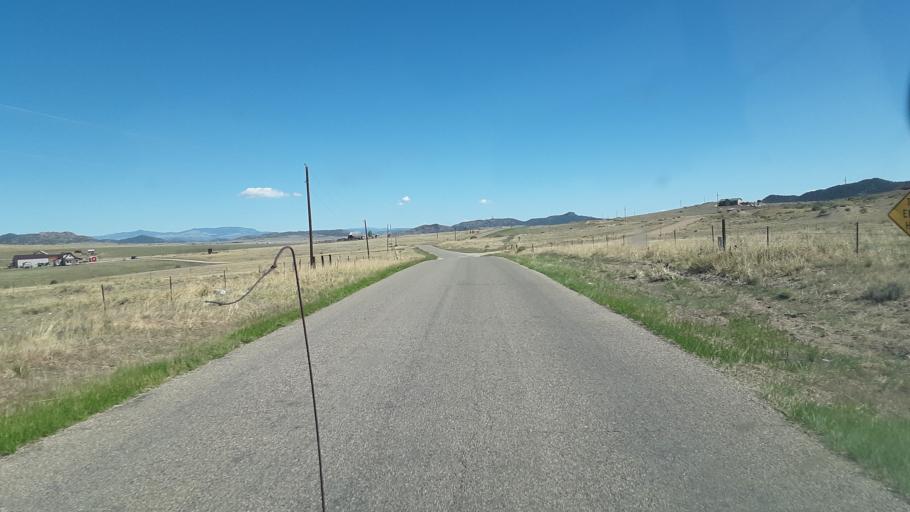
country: US
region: Colorado
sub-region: Custer County
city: Westcliffe
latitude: 38.1555
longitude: -105.4659
